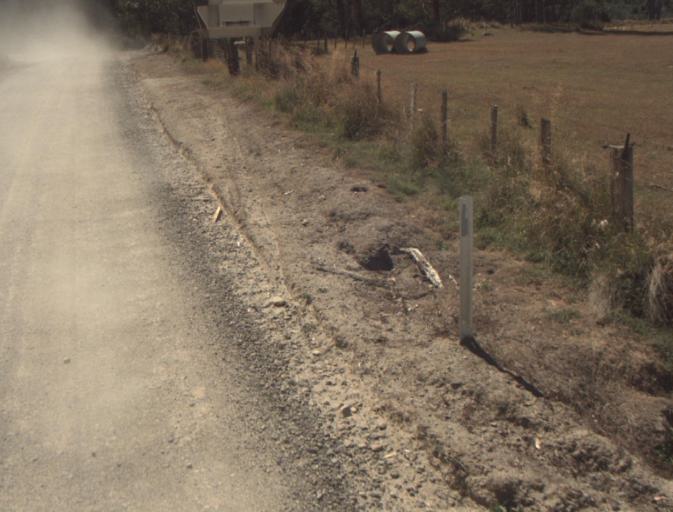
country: AU
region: Tasmania
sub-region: Dorset
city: Scottsdale
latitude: -41.3658
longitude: 147.4673
